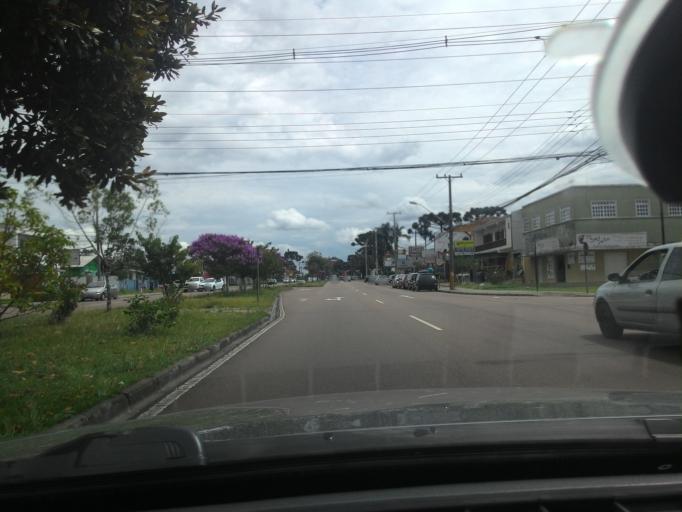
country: BR
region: Parana
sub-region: Pinhais
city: Pinhais
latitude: -25.4566
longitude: -49.2318
